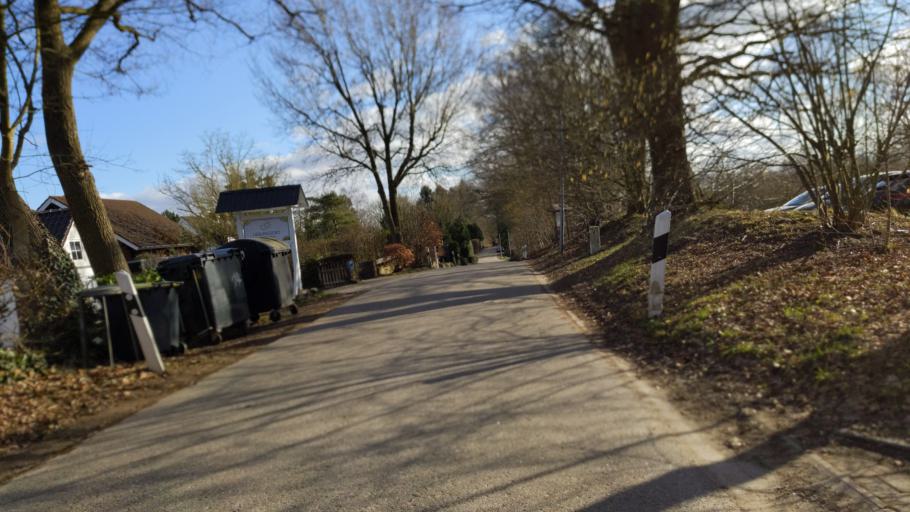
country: DE
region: Schleswig-Holstein
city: Timmendorfer Strand
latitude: 53.9996
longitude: 10.7558
